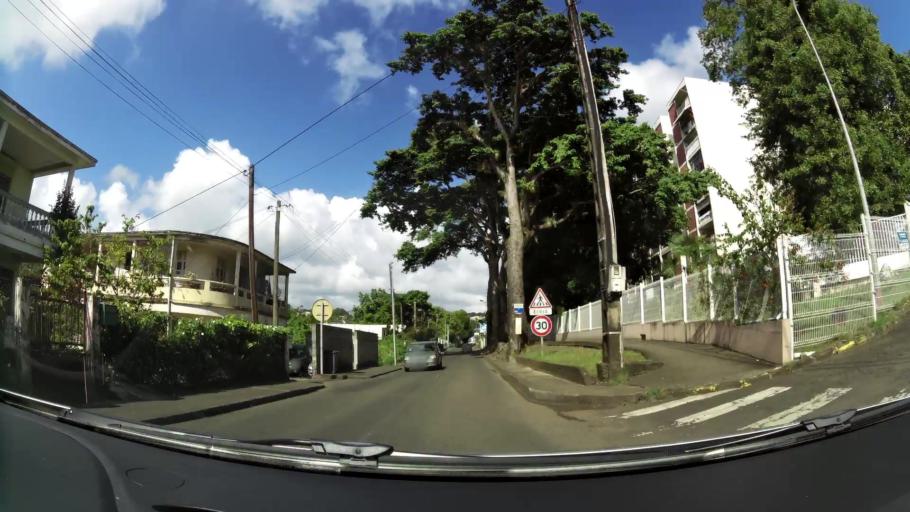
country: MQ
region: Martinique
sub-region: Martinique
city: Fort-de-France
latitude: 14.6129
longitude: -61.0597
